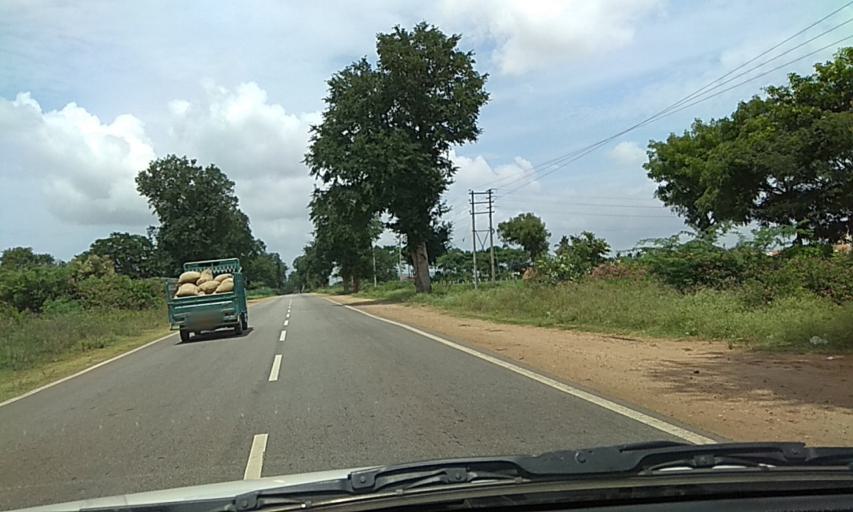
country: IN
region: Karnataka
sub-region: Chamrajnagar
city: Gundlupet
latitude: 11.8106
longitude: 76.7189
